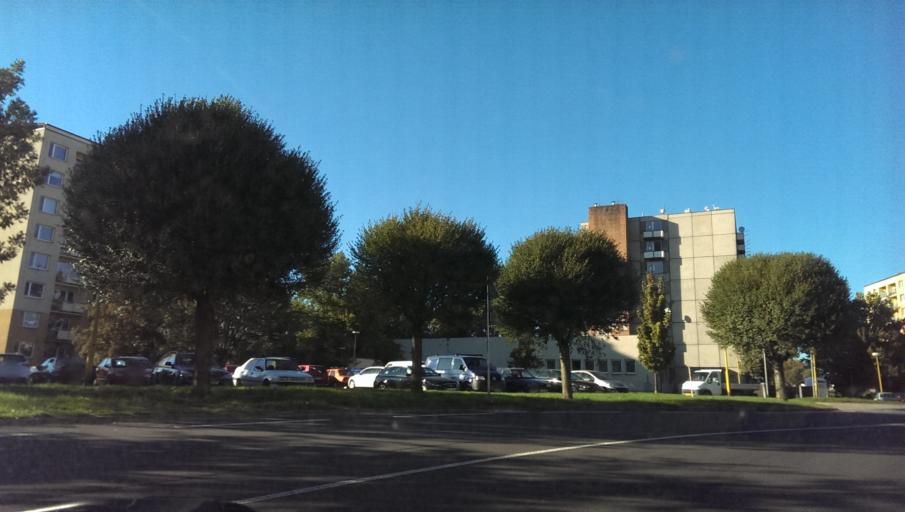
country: CZ
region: Zlin
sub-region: Okres Uherske Hradiste
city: Uherske Hradiste
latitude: 49.0708
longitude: 17.4518
